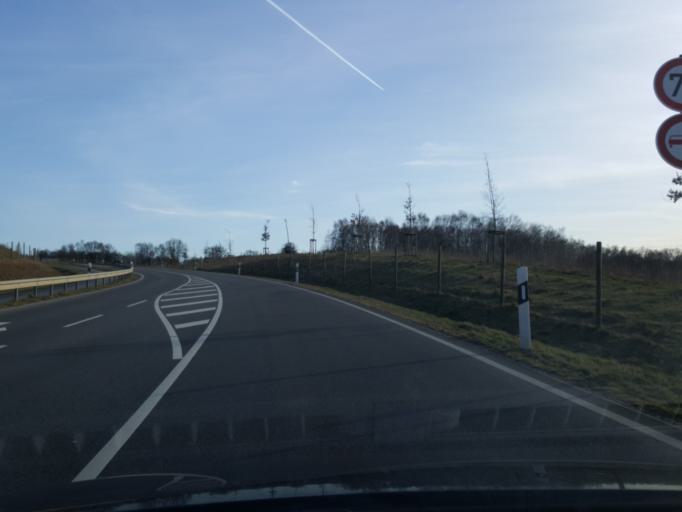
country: DE
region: Lower Saxony
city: Seevetal
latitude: 53.3840
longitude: 9.9703
